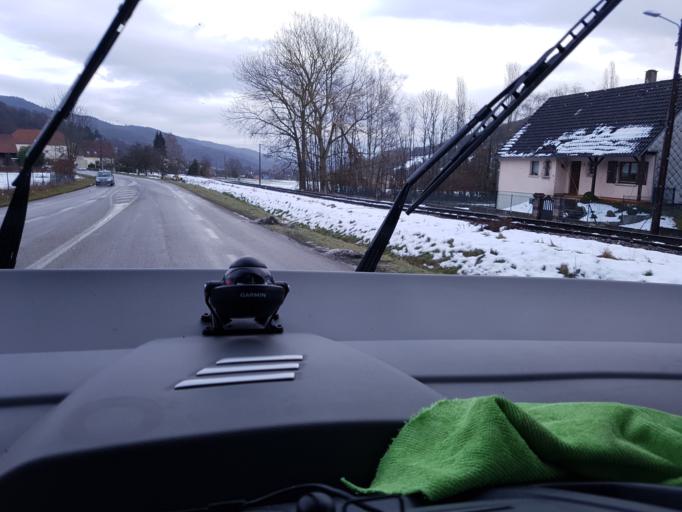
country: FR
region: Alsace
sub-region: Departement du Haut-Rhin
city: Stosswihr
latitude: 48.0309
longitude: 7.1077
